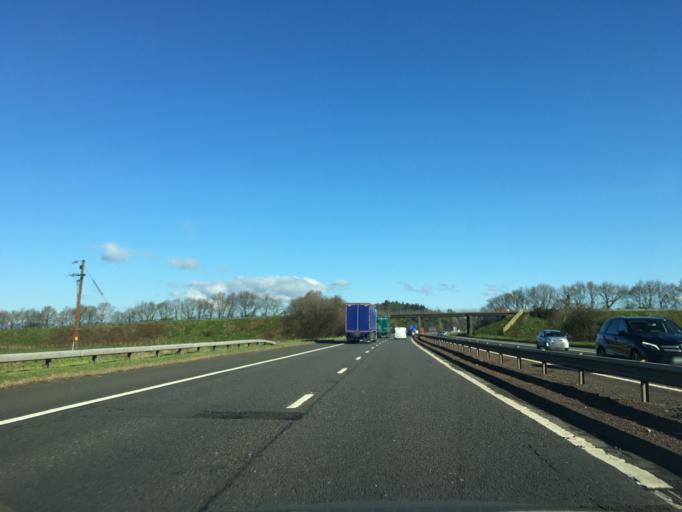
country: GB
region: Scotland
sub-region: Stirling
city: Stirling
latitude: 56.1171
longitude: -3.9681
